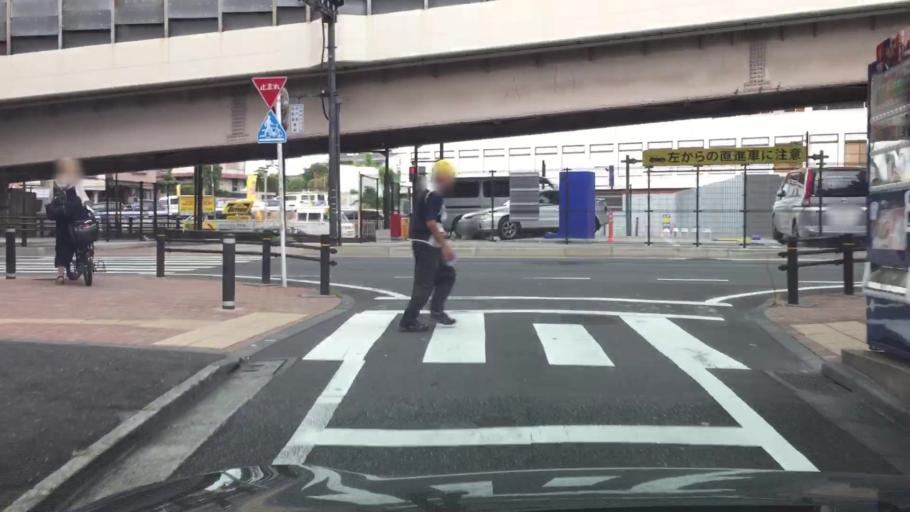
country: JP
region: Tokyo
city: Tokyo
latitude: 35.7363
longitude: 139.7050
